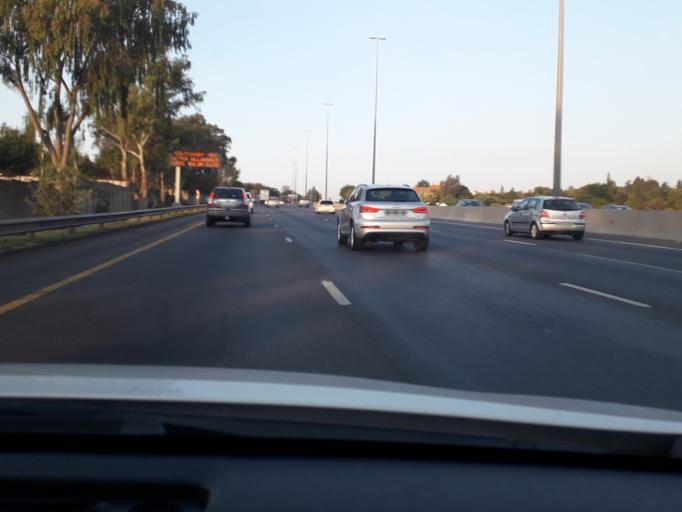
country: ZA
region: Gauteng
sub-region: City of Johannesburg Metropolitan Municipality
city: Diepsloot
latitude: -26.0441
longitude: 28.0037
